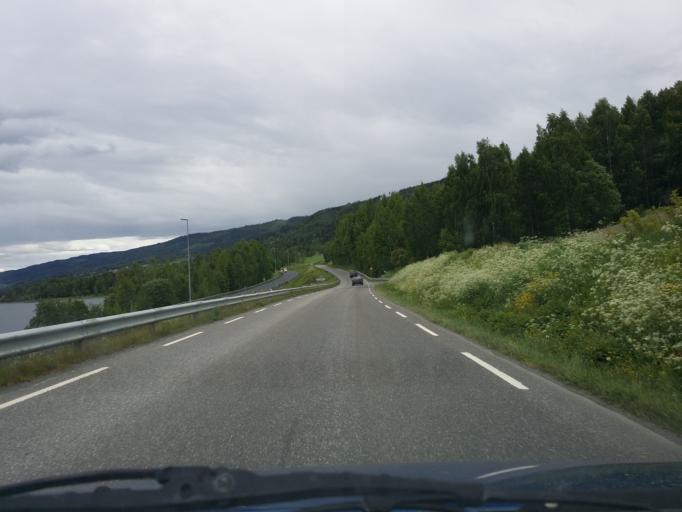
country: NO
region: Oppland
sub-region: Lillehammer
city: Lillehammer
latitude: 61.0331
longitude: 10.4415
